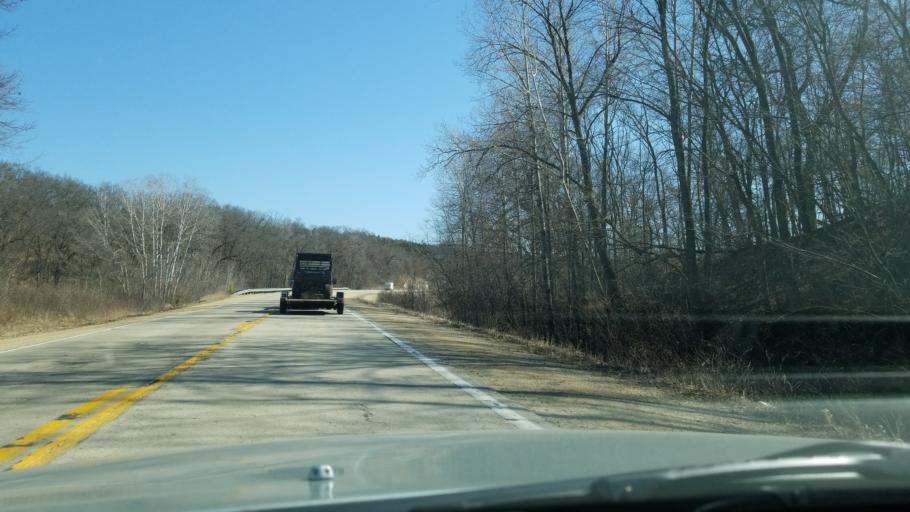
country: US
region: Wisconsin
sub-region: Iowa County
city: Mineral Point
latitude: 42.8767
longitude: -90.2105
